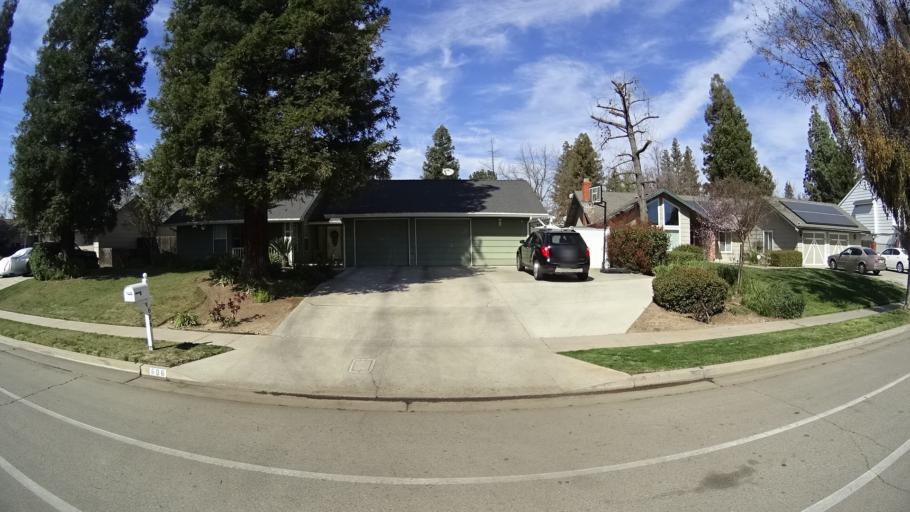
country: US
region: California
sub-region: Fresno County
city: Clovis
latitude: 36.8622
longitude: -119.7724
